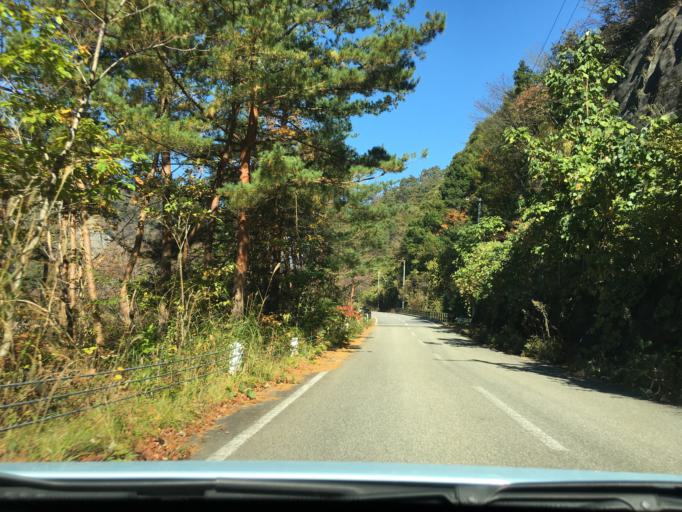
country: JP
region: Fukushima
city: Inawashiro
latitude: 37.4516
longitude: 139.9667
